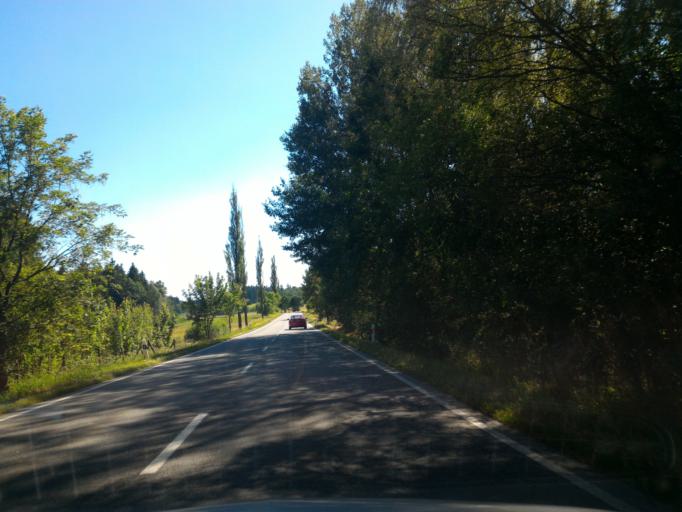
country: CZ
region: Vysocina
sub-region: Okres Jihlava
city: Trest'
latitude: 49.2461
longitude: 15.4676
